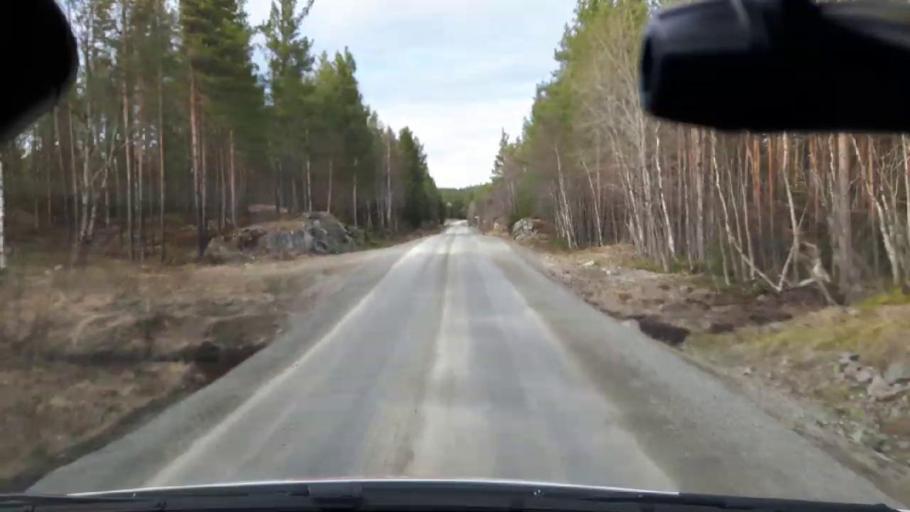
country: SE
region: Jaemtland
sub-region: Bergs Kommun
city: Hoverberg
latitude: 62.9300
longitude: 14.6477
